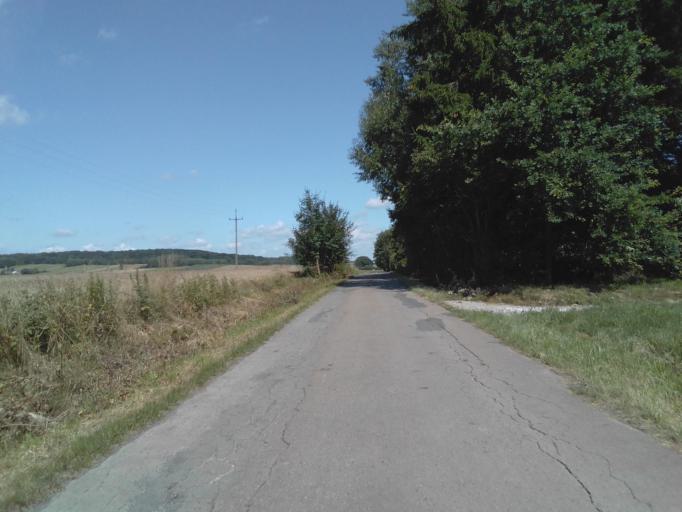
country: PL
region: Subcarpathian Voivodeship
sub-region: Powiat krosnienski
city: Wojaszowka
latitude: 49.7604
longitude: 21.6435
